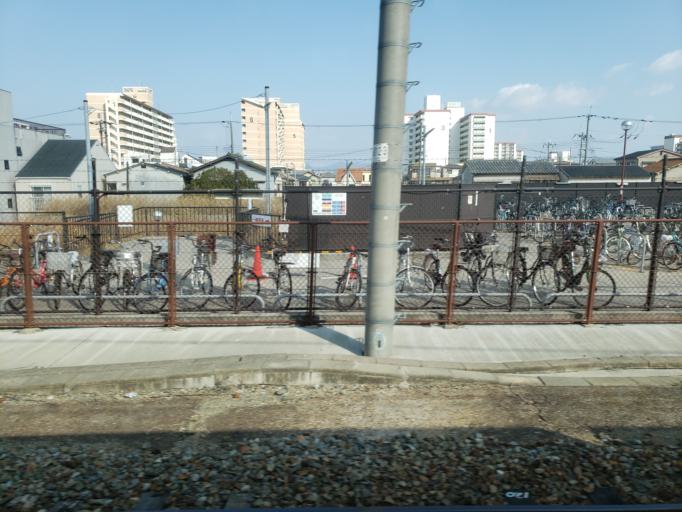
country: JP
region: Hyogo
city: Nishinomiya-hama
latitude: 34.7393
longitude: 135.3483
